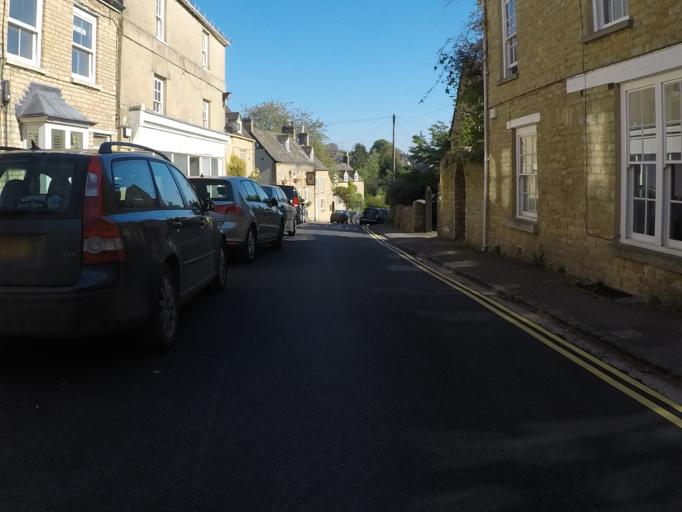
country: GB
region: England
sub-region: Oxfordshire
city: Charlbury
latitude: 51.8723
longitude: -1.4816
